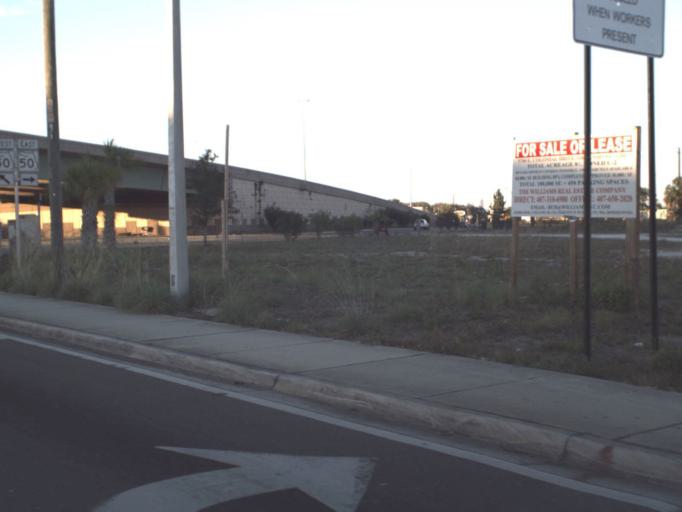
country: US
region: Florida
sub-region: Orange County
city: Azalea Park
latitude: 28.5564
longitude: -81.3107
